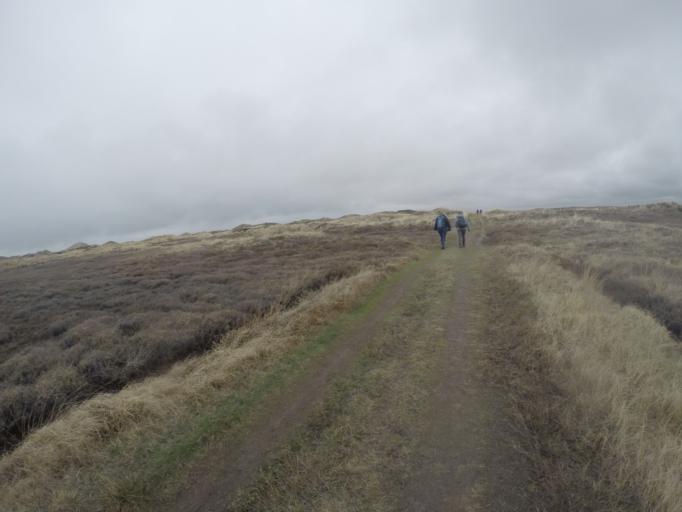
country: DK
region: North Denmark
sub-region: Thisted Kommune
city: Hurup
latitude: 56.8525
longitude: 8.2875
